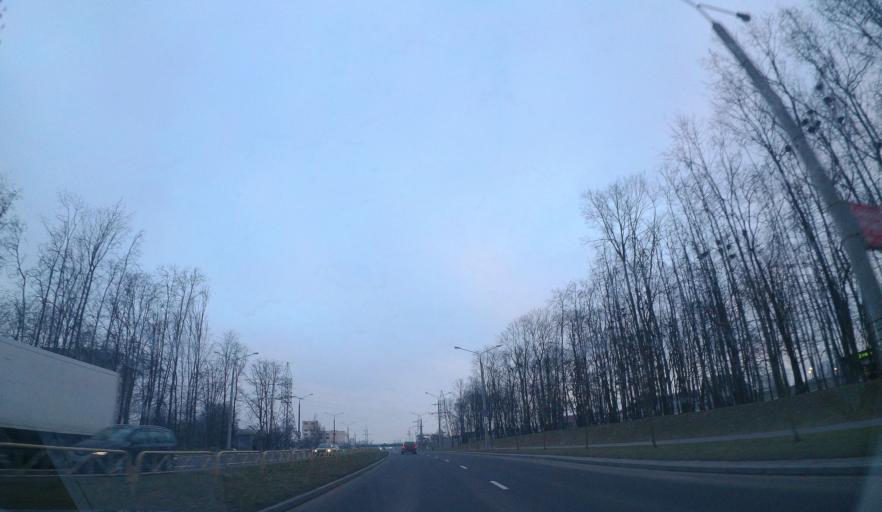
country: BY
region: Grodnenskaya
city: Hrodna
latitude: 53.6559
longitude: 23.7841
